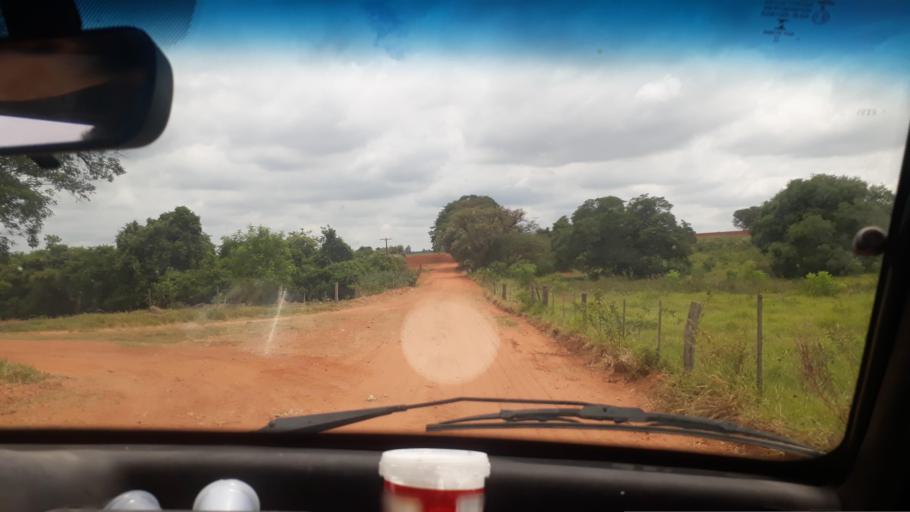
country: BR
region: Sao Paulo
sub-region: Regente Feijo
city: Regente Feijo
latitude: -22.2515
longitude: -51.2988
